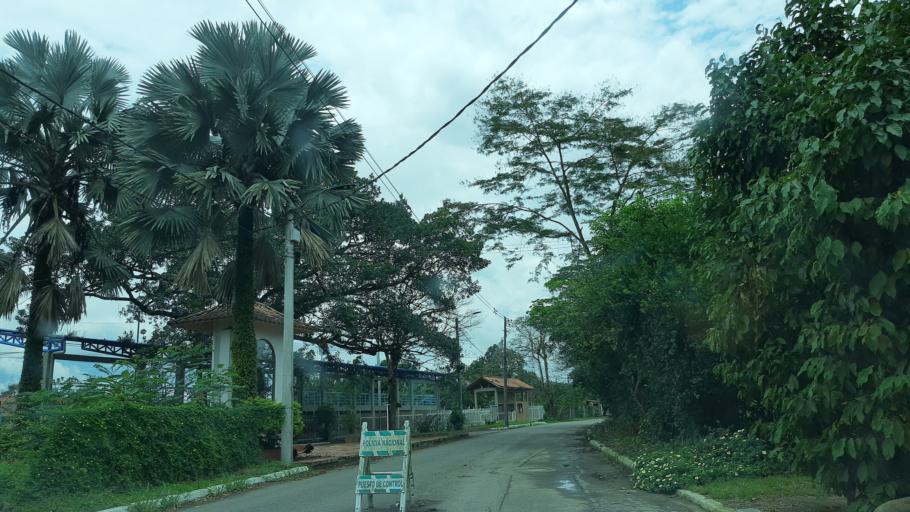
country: CO
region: Casanare
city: Sabanalarga
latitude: 4.8506
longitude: -73.0410
